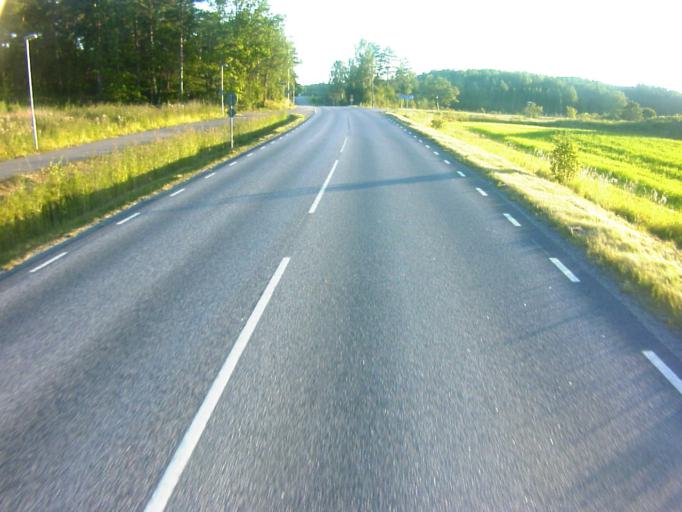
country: SE
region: Soedermanland
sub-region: Eskilstuna Kommun
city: Torshalla
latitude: 59.4155
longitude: 16.4452
